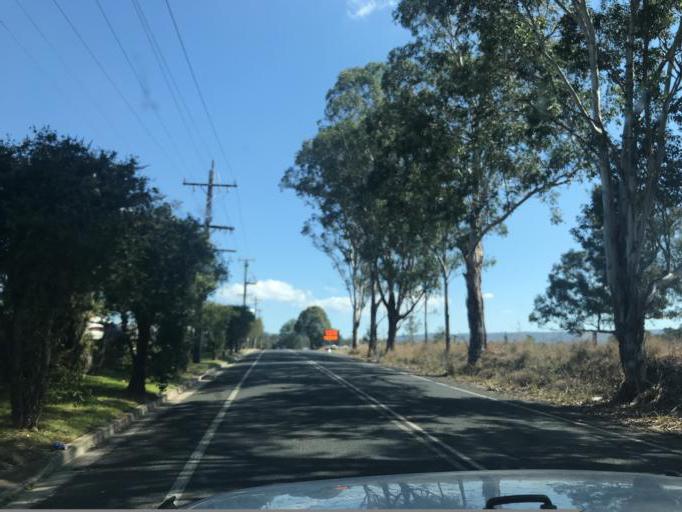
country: AU
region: New South Wales
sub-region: Hawkesbury
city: Richmond
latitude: -33.5777
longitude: 150.7238
